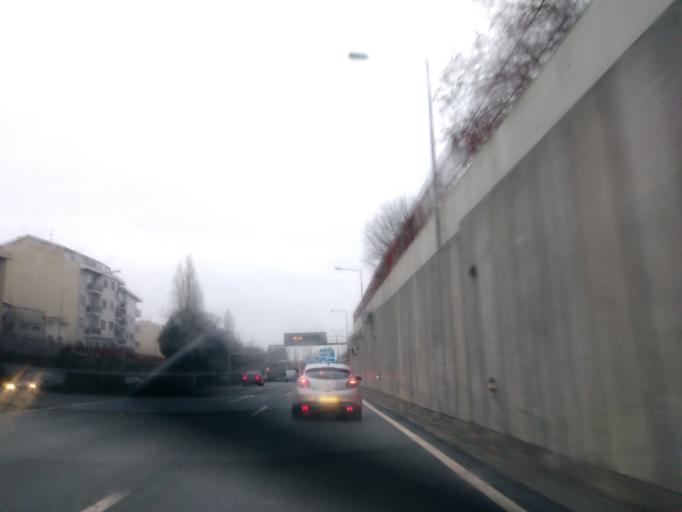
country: PT
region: Porto
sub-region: Maia
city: Pedroucos
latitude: 41.1700
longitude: -8.5917
